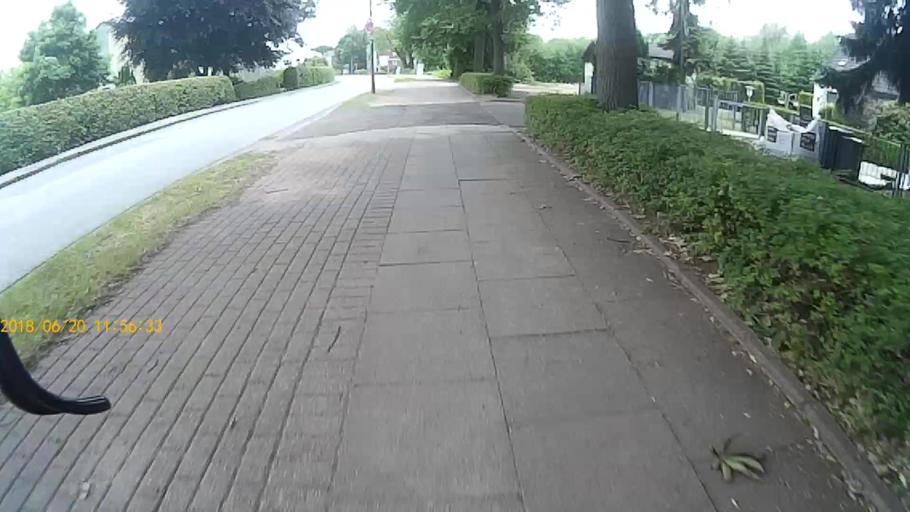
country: DE
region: Hamburg
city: Rothenburgsort
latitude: 53.5097
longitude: 10.0211
